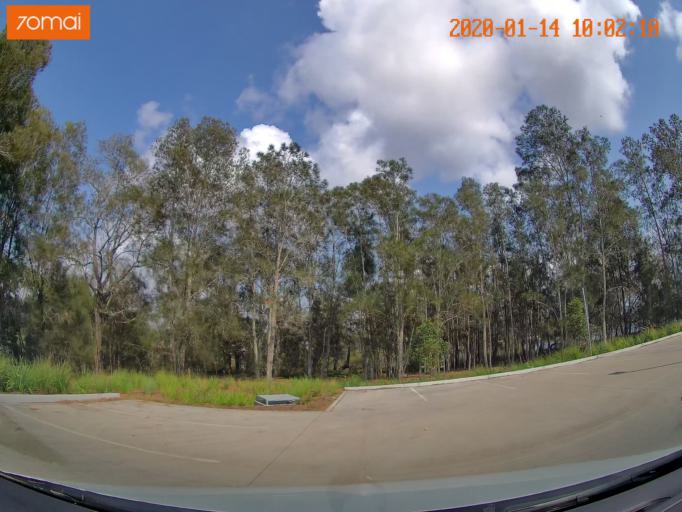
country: AU
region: New South Wales
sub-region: Wyong Shire
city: Kingfisher Shores
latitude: -33.1230
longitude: 151.5398
